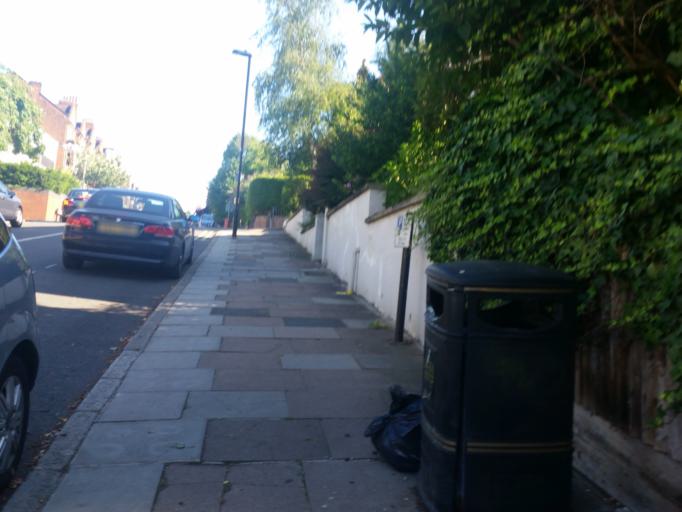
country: GB
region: England
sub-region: Greater London
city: Crouch End
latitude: 51.5803
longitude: -0.1325
